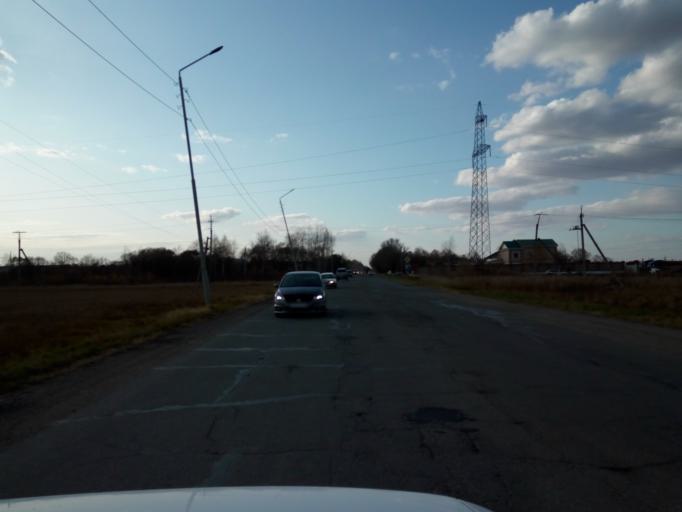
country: RU
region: Primorskiy
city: Dal'nerechensk
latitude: 45.9170
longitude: 133.7645
